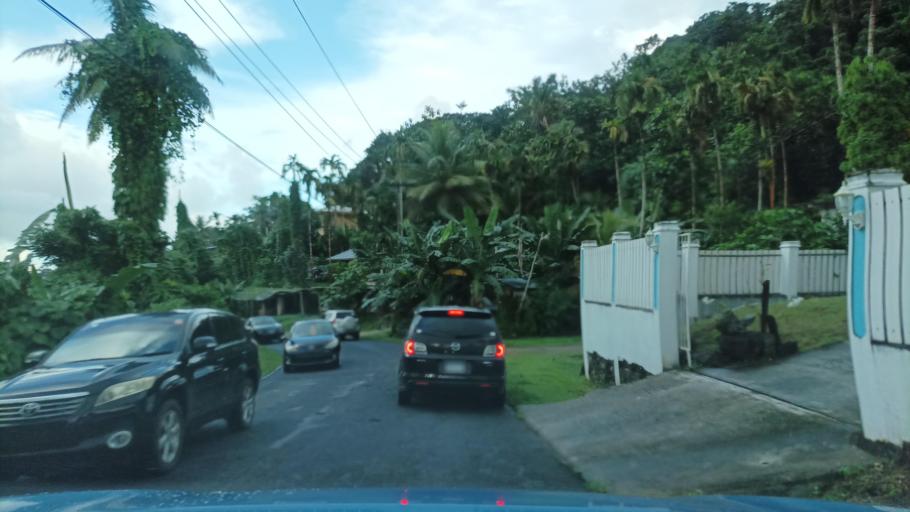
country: FM
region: Pohnpei
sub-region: Kolonia Municipality
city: Kolonia Town
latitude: 6.9554
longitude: 158.1978
